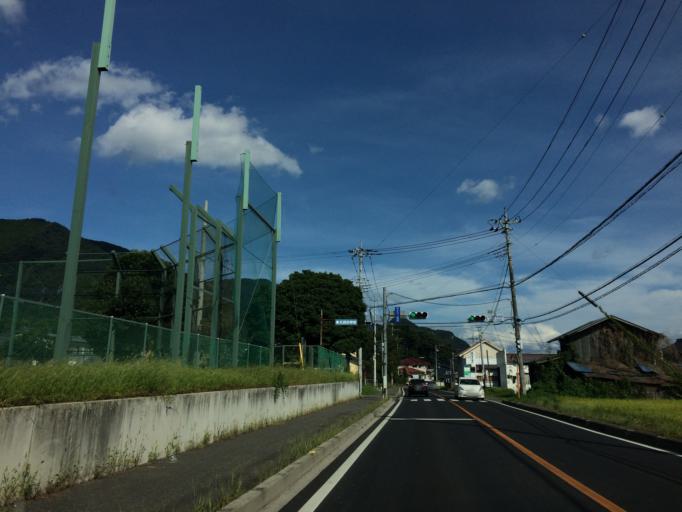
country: JP
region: Gunma
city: Nakanojomachi
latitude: 36.5725
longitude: 138.8649
